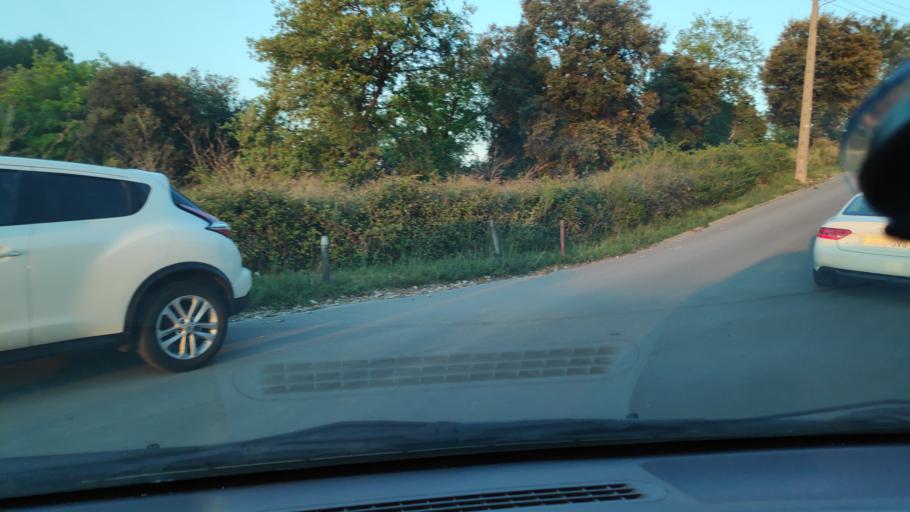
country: ES
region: Catalonia
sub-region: Provincia de Barcelona
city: Sant Quirze del Valles
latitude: 41.5335
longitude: 2.0491
